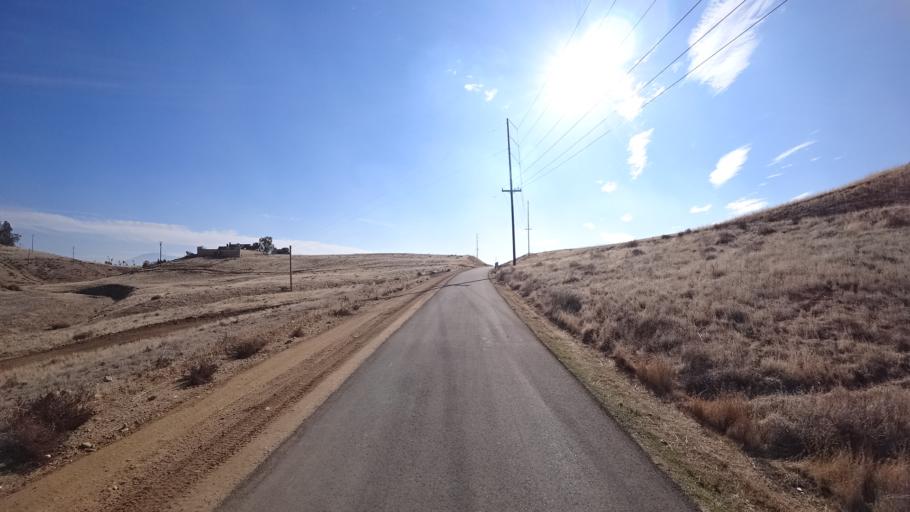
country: US
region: California
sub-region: Kern County
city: Oildale
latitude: 35.4210
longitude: -118.9013
